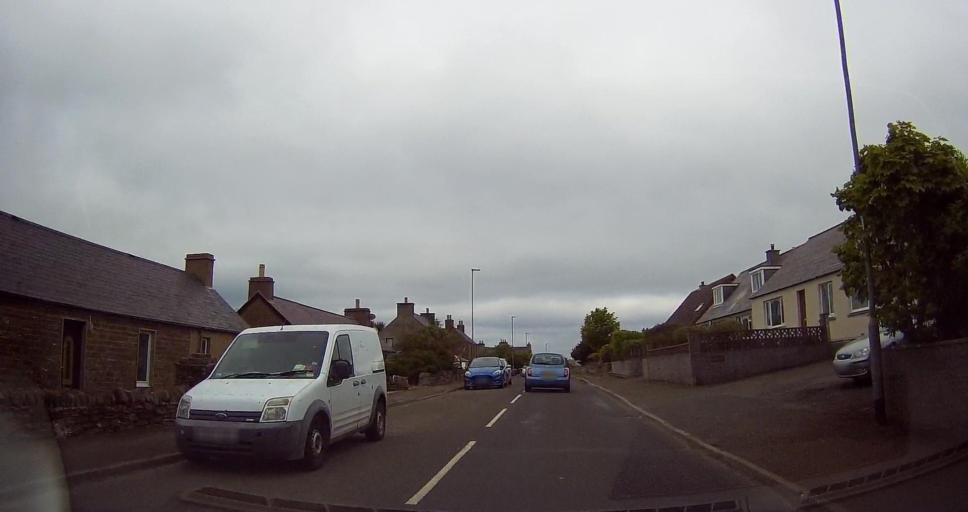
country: GB
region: Scotland
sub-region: Orkney Islands
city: Kirkwall
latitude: 58.9742
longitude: -2.9535
